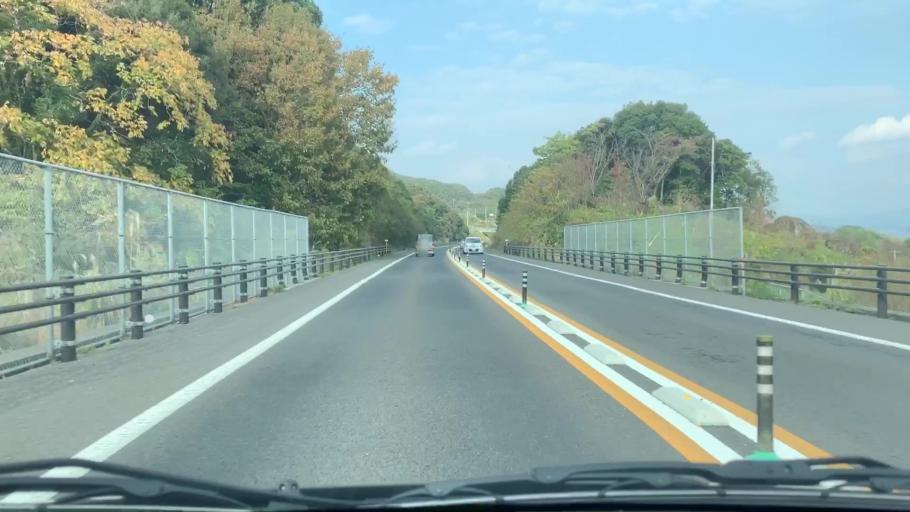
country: JP
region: Nagasaki
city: Sasebo
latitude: 33.0162
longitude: 129.7312
